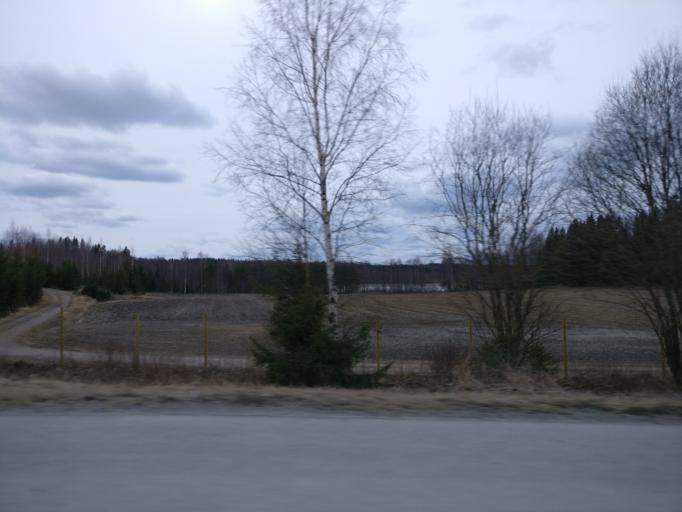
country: FI
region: Haeme
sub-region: Haemeenlinna
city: Janakkala
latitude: 60.8919
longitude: 24.5618
